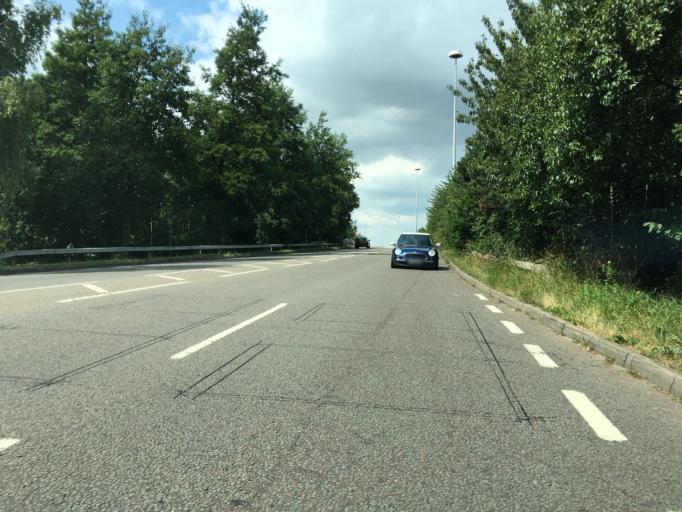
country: GB
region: England
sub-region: Gloucestershire
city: Barnwood
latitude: 51.8585
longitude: -2.2213
